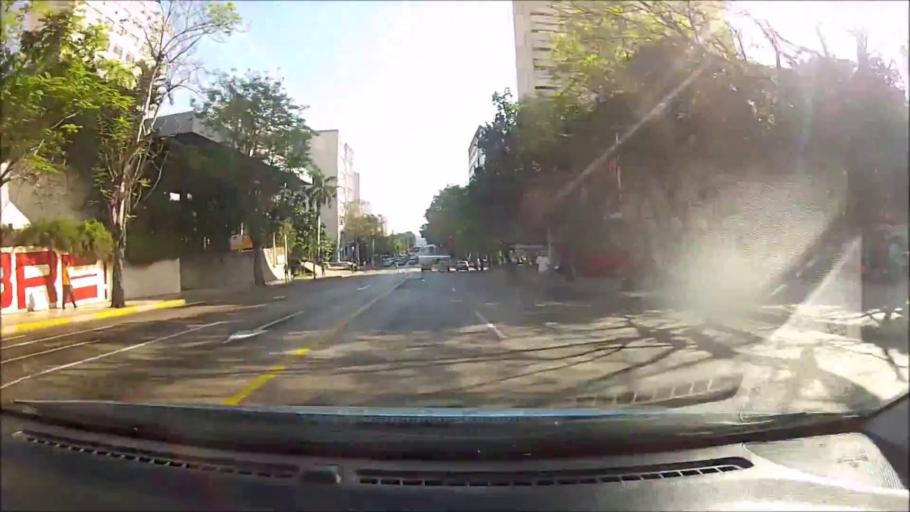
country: CU
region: La Habana
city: Havana
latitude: 23.1386
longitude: -82.3847
